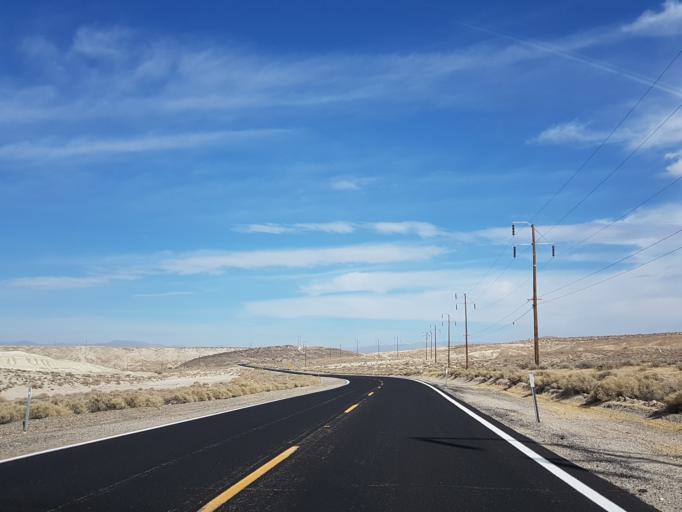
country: US
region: California
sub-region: San Bernardino County
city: Searles Valley
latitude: 35.6511
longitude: -117.4688
